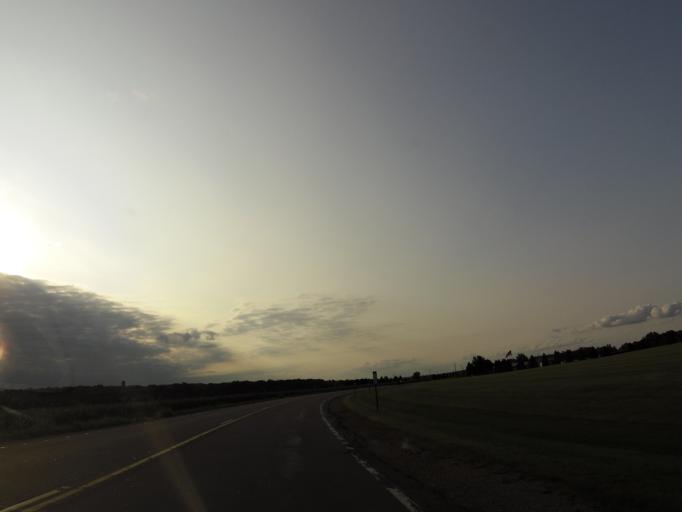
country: US
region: Minnesota
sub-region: Dakota County
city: Farmington
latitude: 44.6188
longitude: -93.0114
